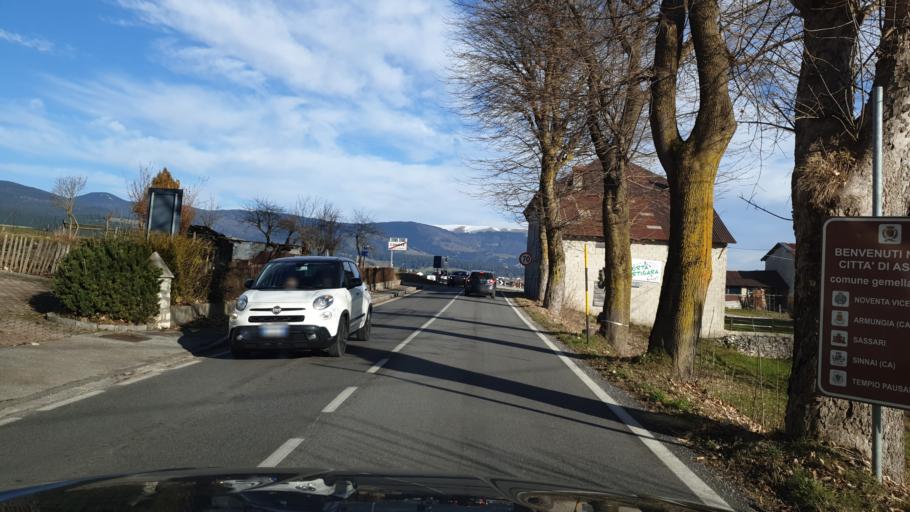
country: IT
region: Veneto
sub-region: Provincia di Vicenza
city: Canove di Roana
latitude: 45.8693
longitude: 11.4885
